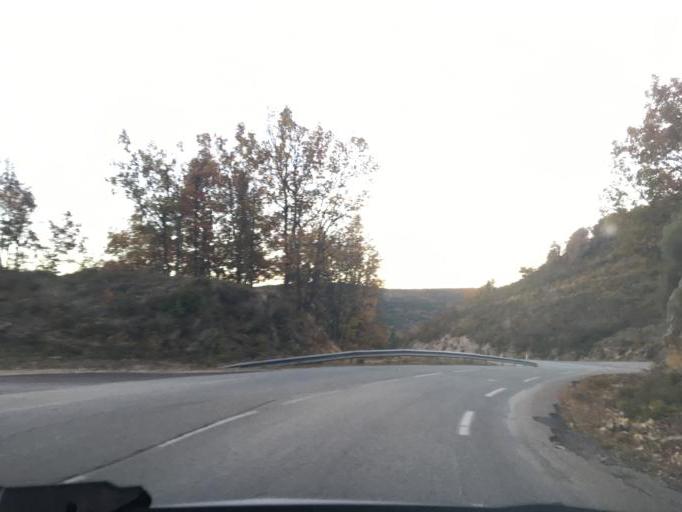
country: FR
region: Provence-Alpes-Cote d'Azur
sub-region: Departement du Var
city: Bargemon
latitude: 43.6837
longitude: 6.5111
